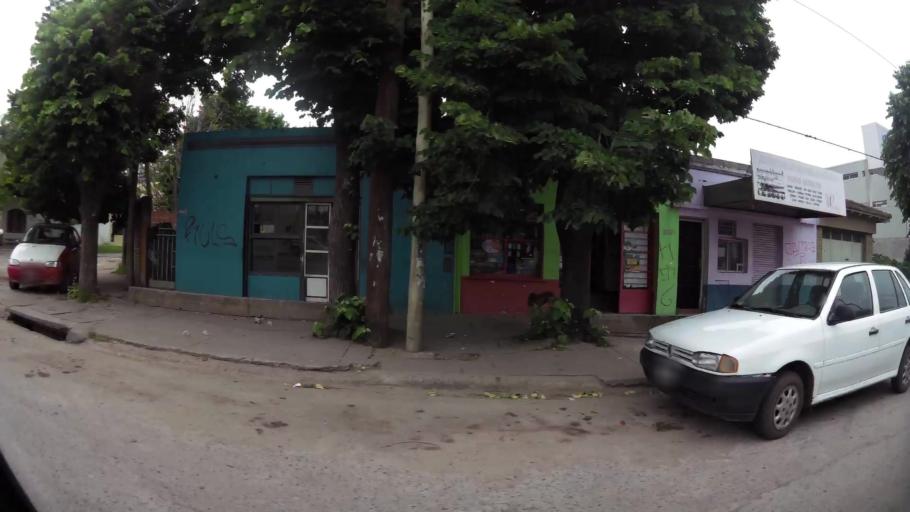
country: AR
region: Buenos Aires
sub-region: Partido de La Plata
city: La Plata
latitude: -34.9515
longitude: -58.0000
